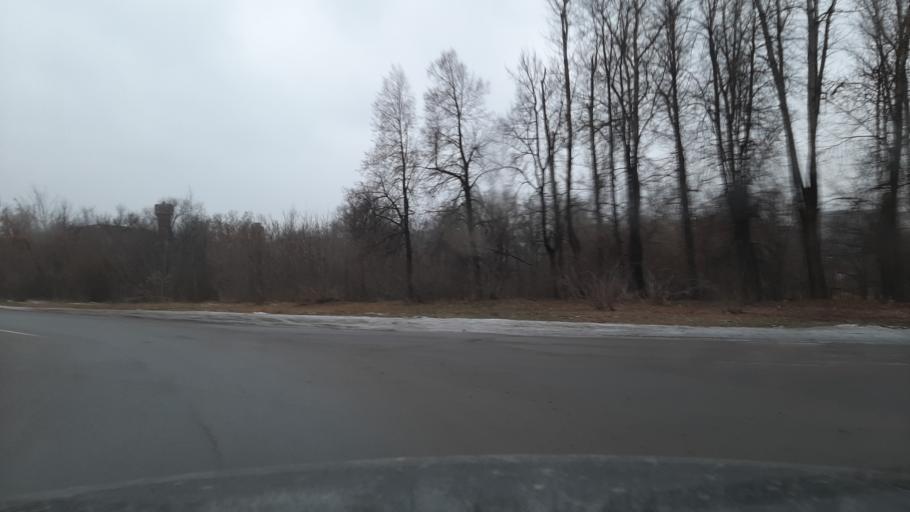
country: RU
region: Ivanovo
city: Shuya
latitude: 56.8576
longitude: 41.3599
